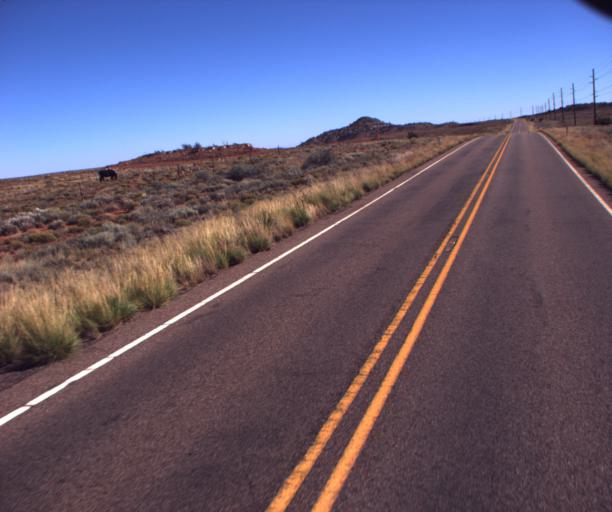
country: US
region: Arizona
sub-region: Navajo County
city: Taylor
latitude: 34.4923
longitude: -110.2203
